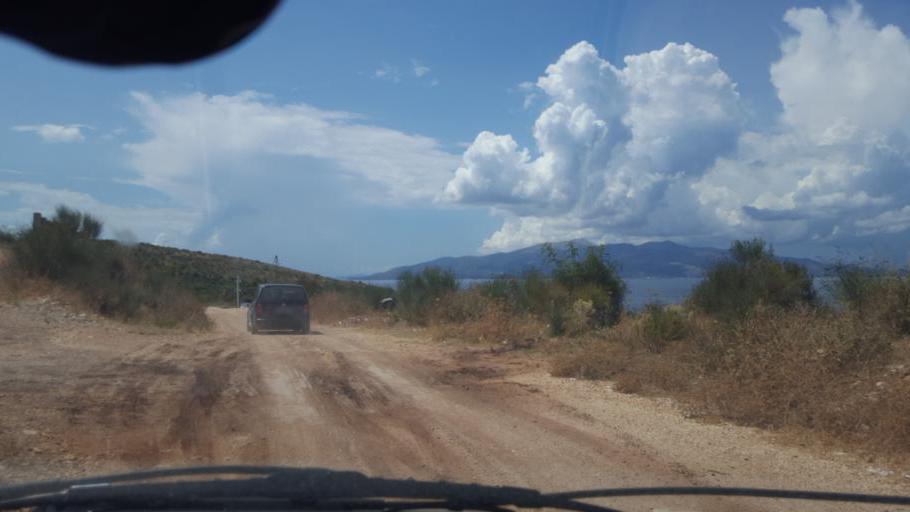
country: AL
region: Vlore
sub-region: Rrethi i Sarandes
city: Sarande
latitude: 39.8400
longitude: 20.0129
